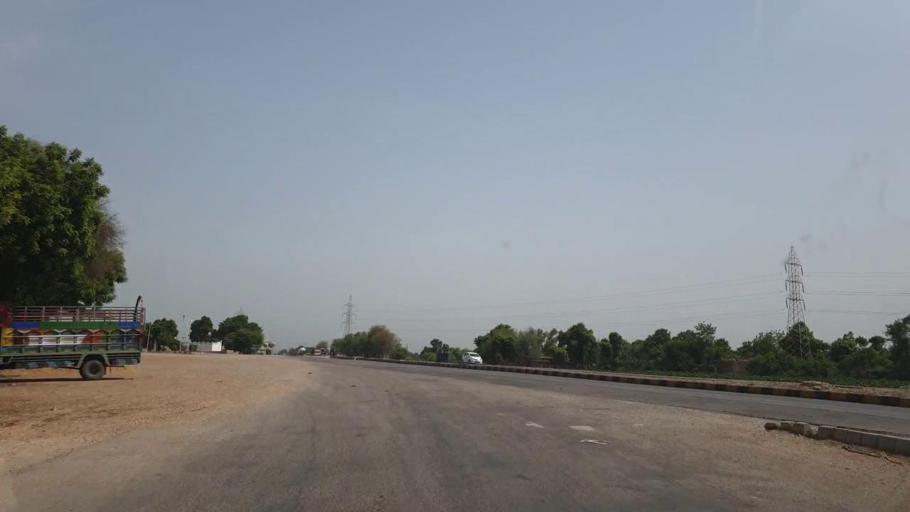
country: PK
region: Sindh
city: Sakrand
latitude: 26.1545
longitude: 68.2513
